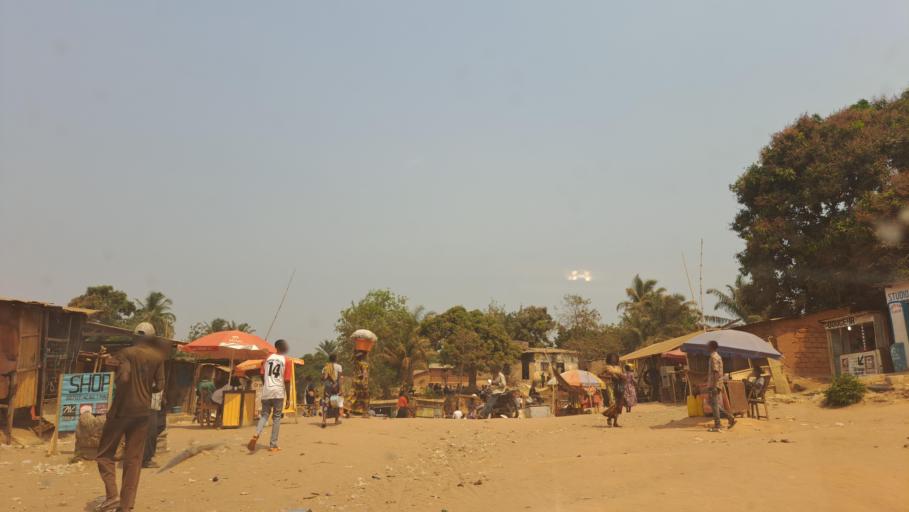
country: CD
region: Kasai-Oriental
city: Mbuji-Mayi
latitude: -6.1065
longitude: 23.5604
